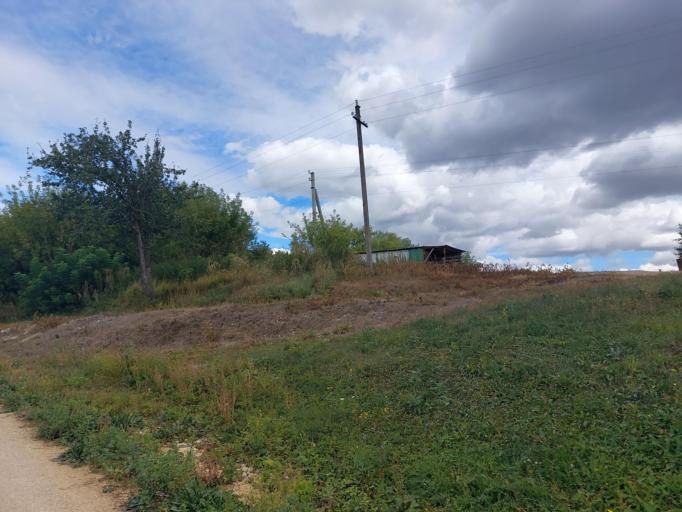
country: RU
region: Lipetsk
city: Terbuny
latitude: 52.2639
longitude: 38.2066
